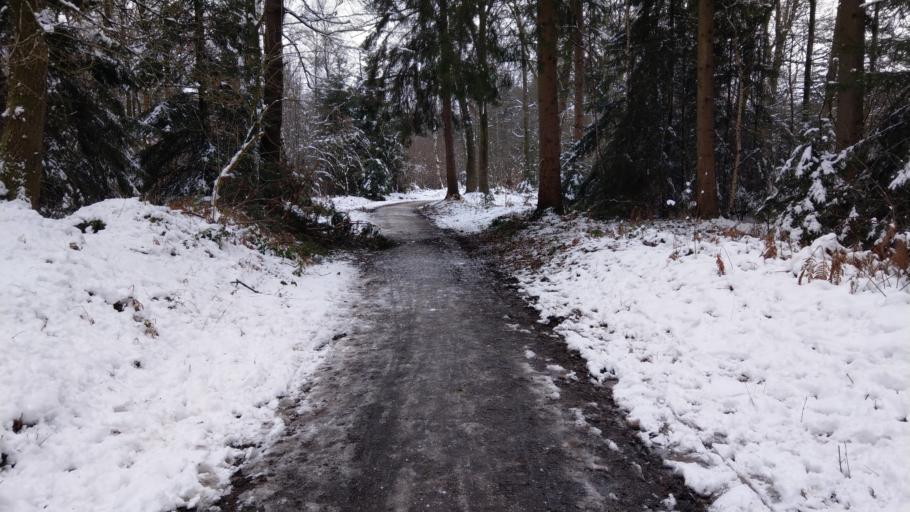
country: BE
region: Wallonia
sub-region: Province de Liege
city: Raeren
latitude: 50.7157
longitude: 6.0984
